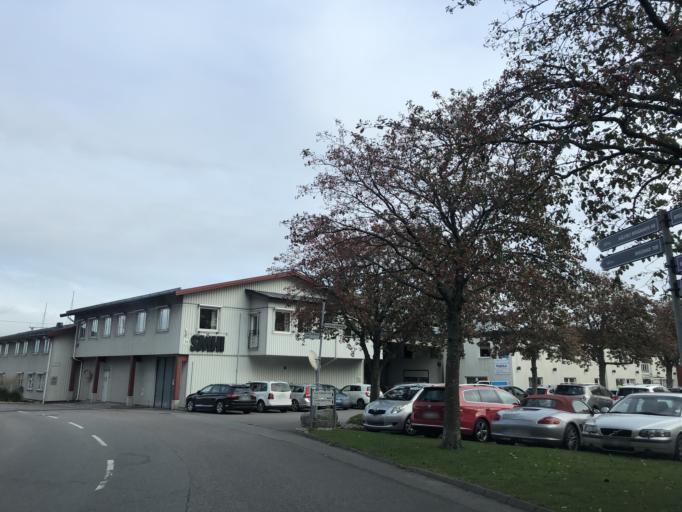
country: SE
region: Vaestra Goetaland
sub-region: Goteborg
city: Majorna
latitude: 57.6839
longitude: 11.8898
